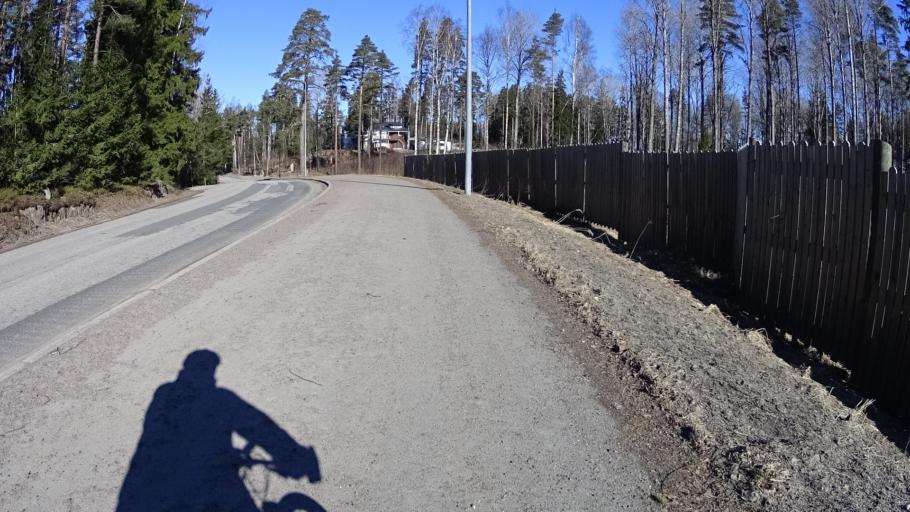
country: FI
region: Uusimaa
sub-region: Helsinki
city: Kauniainen
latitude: 60.2551
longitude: 24.7063
